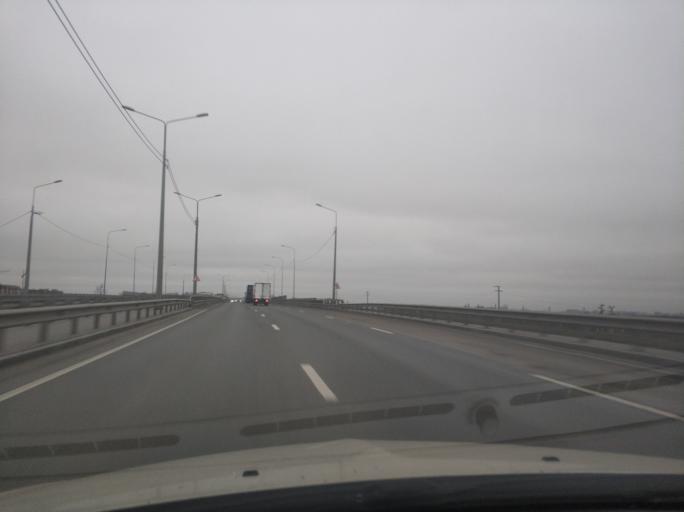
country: RU
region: St.-Petersburg
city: Pushkin
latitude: 59.7552
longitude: 30.3857
